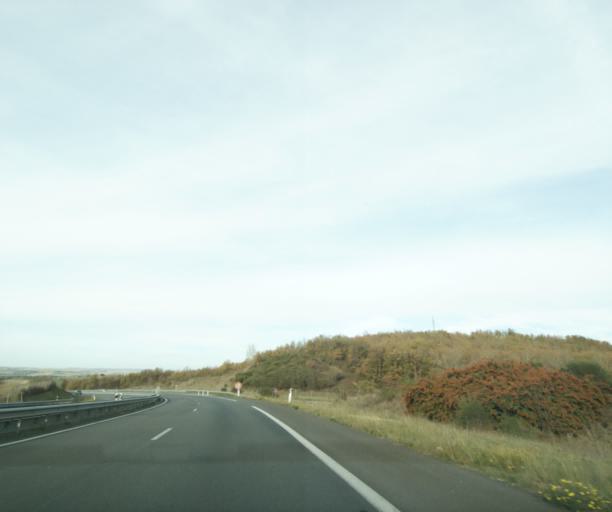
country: FR
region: Midi-Pyrenees
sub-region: Departement du Gers
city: Pujaudran
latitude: 43.5907
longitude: 1.1268
